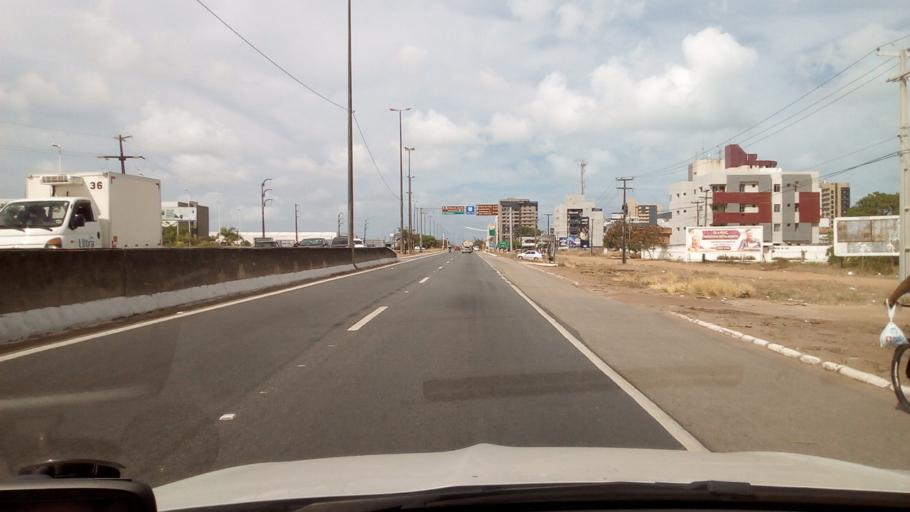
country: BR
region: Paraiba
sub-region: Cabedelo
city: Cabedelo
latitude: -7.0467
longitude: -34.8478
